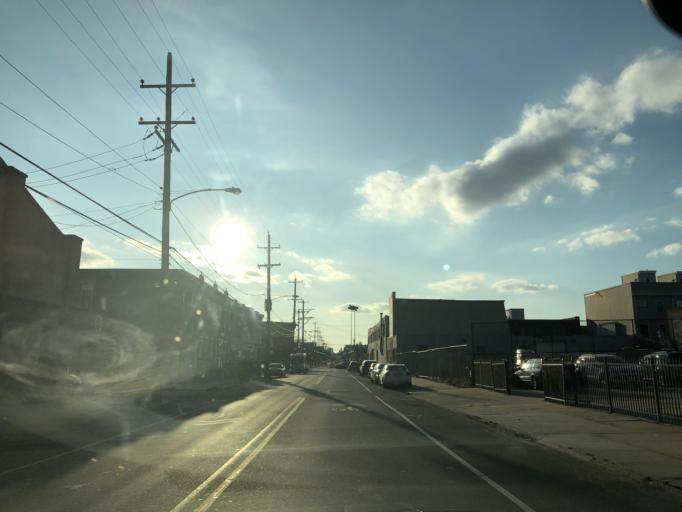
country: US
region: New Jersey
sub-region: Camden County
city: Merchantville
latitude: 39.9850
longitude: -75.0976
